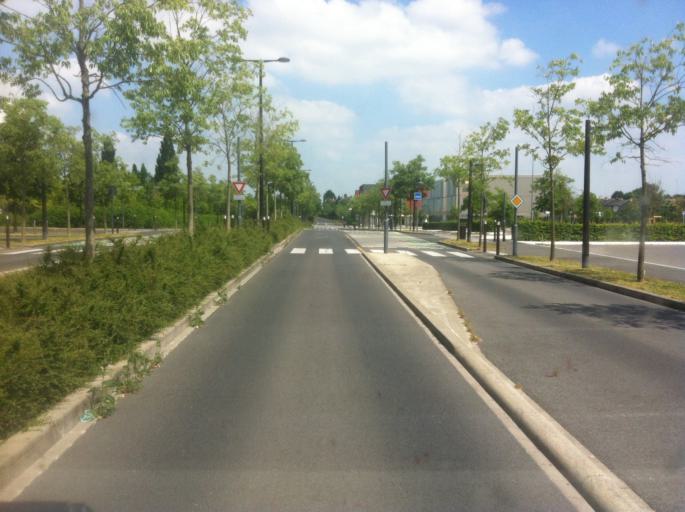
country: FR
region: Nord-Pas-de-Calais
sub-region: Departement du Nord
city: Maubeuge
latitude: 50.2901
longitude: 3.9654
